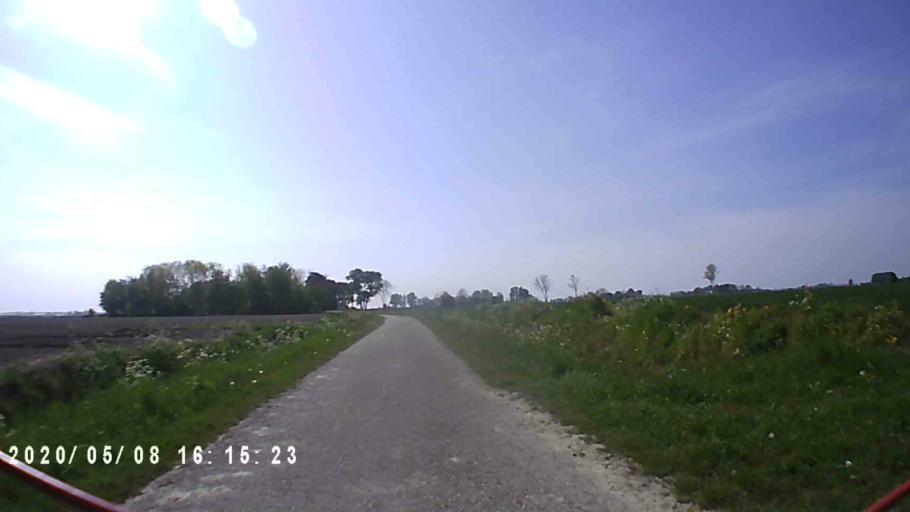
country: NL
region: Groningen
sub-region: Gemeente Bedum
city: Bedum
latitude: 53.3787
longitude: 6.6826
